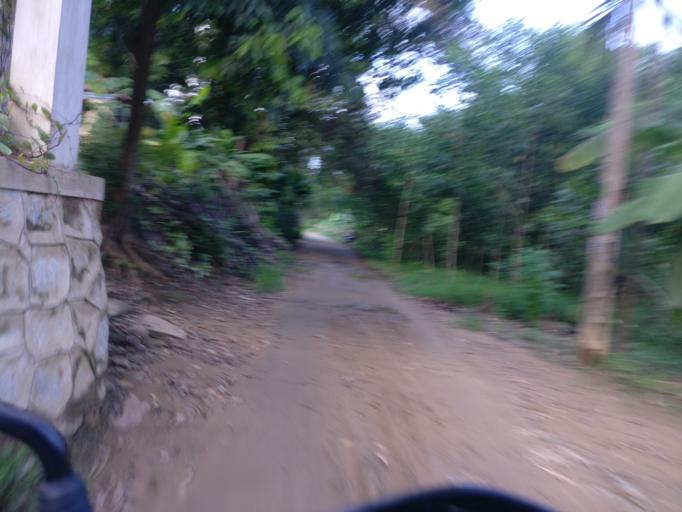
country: VN
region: Thua Thien-Hue
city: Hue
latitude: 16.3900
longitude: 107.5744
